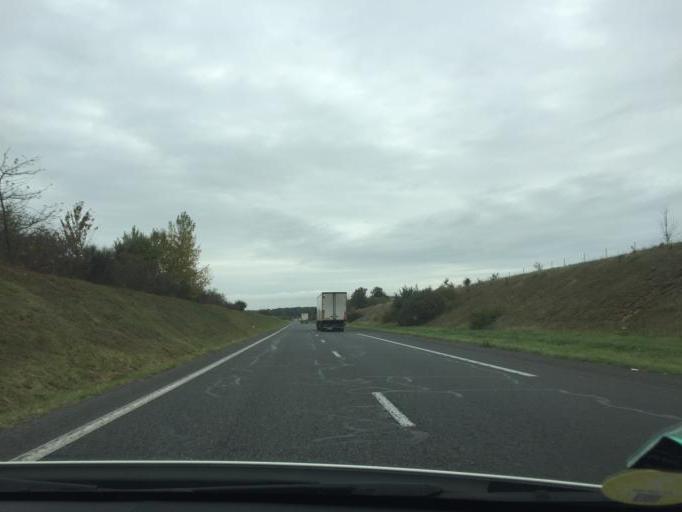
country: FR
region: Bourgogne
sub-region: Departement de l'Yonne
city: Egriselles-le-Bocage
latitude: 48.0831
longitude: 3.1296
